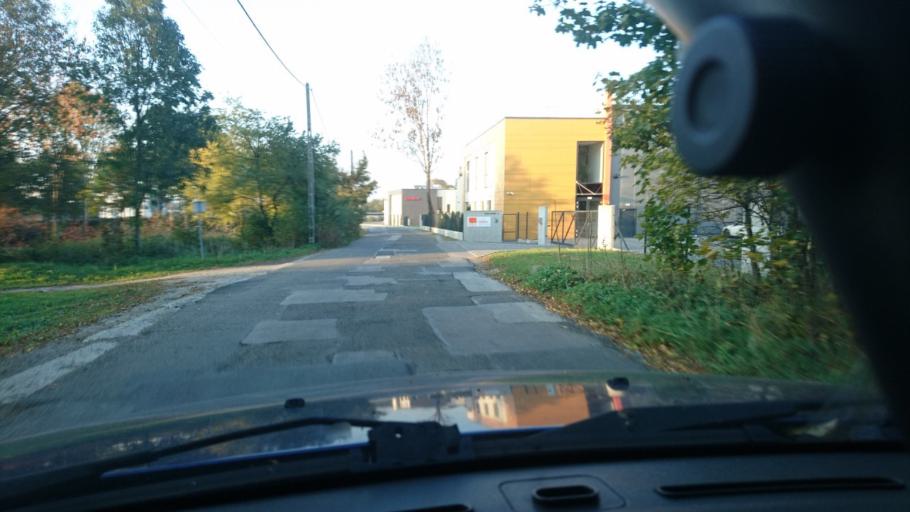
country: PL
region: Silesian Voivodeship
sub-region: Powiat bielski
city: Mazancowice
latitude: 49.8221
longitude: 18.9803
